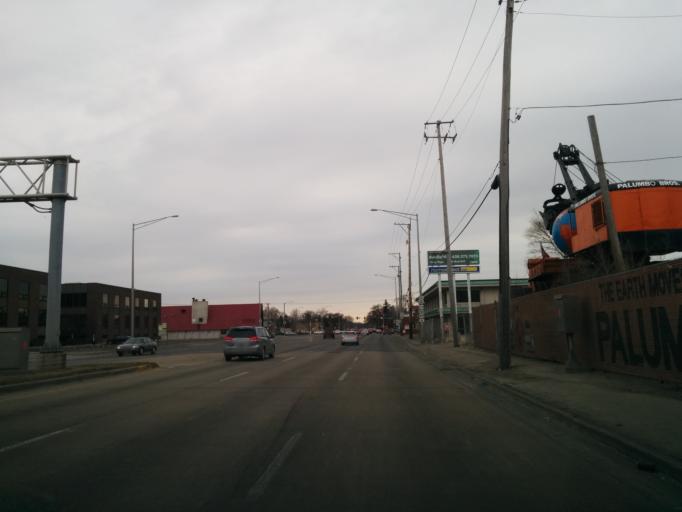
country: US
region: Illinois
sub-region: Cook County
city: Westchester
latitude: 41.8655
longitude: -87.8827
